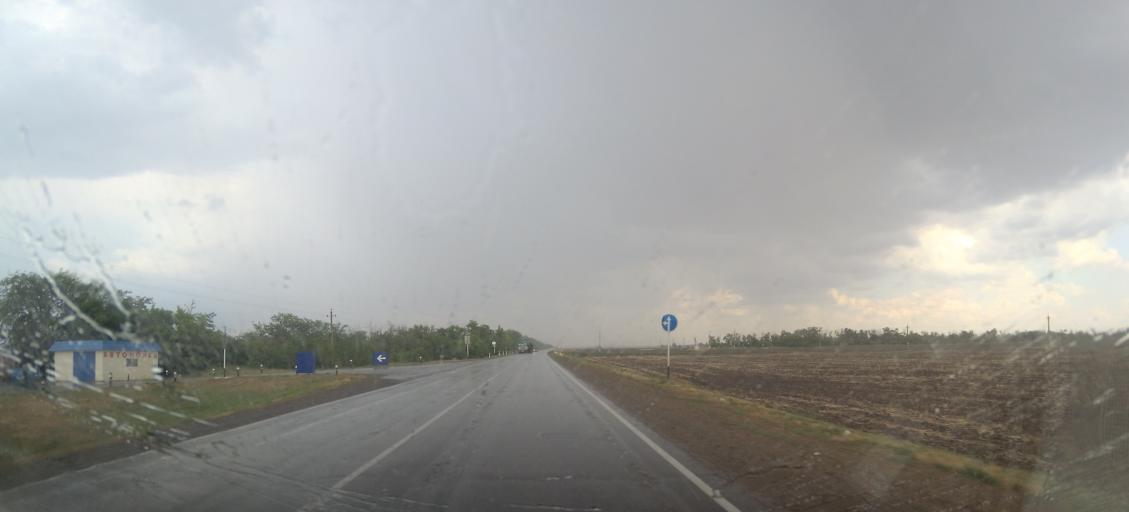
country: RU
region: Rostov
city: Proletarsk
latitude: 46.6484
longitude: 41.6759
